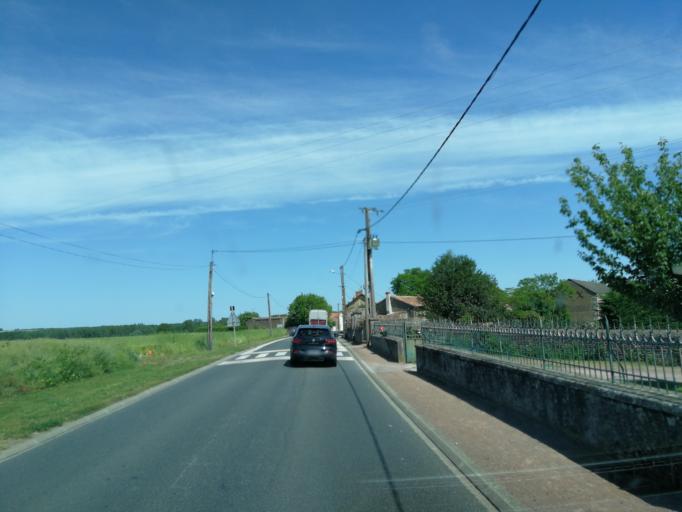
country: FR
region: Poitou-Charentes
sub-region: Departement des Deux-Sevres
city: Saint-Leger-de-Montbrun
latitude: 46.9758
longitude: -0.0467
